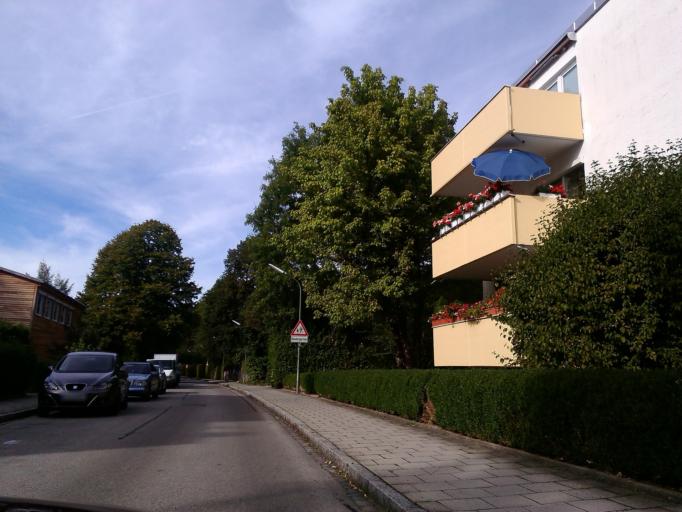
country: DE
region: Bavaria
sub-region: Upper Bavaria
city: Pullach im Isartal
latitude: 48.0747
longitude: 11.5202
